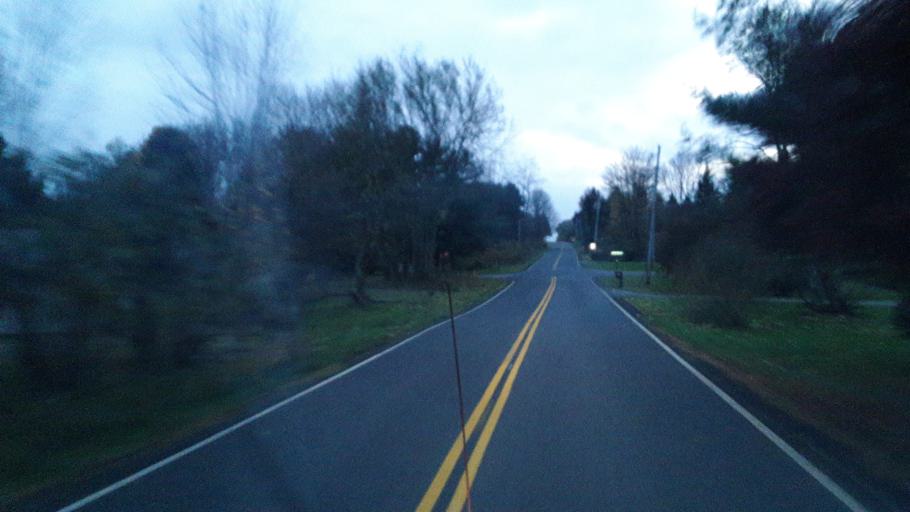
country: US
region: Ohio
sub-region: Portage County
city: Mantua
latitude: 41.2933
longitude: -81.2608
